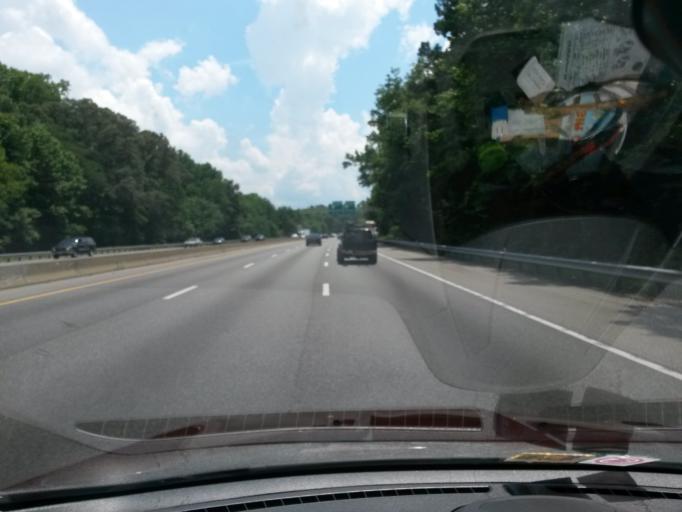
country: US
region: Virginia
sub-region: Chesterfield County
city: Chester
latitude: 37.3698
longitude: -77.4042
